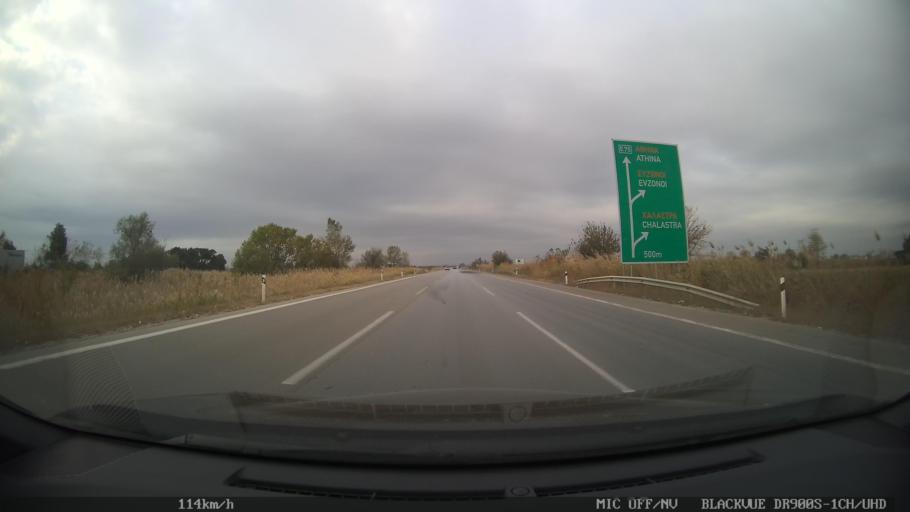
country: GR
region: Central Macedonia
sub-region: Nomos Thessalonikis
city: Chalastra
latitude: 40.6195
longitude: 22.7532
